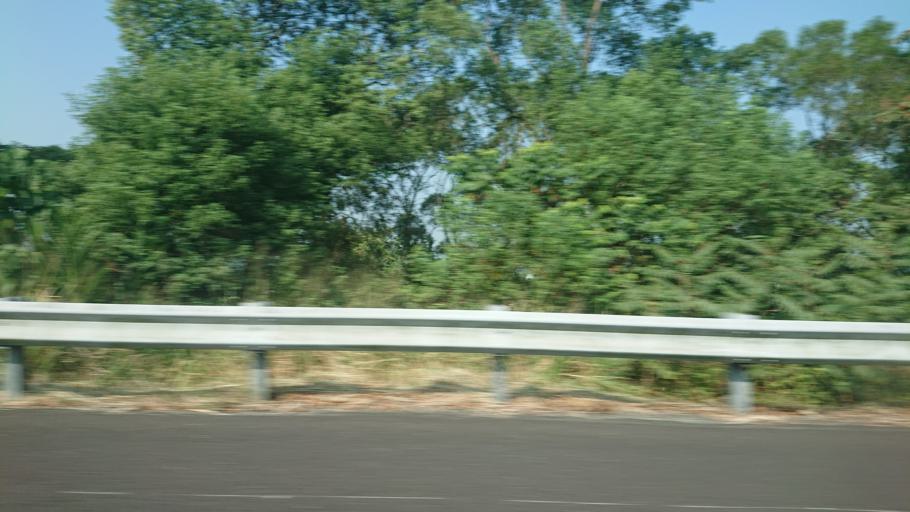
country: TW
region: Taiwan
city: Lugu
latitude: 23.8213
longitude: 120.7058
